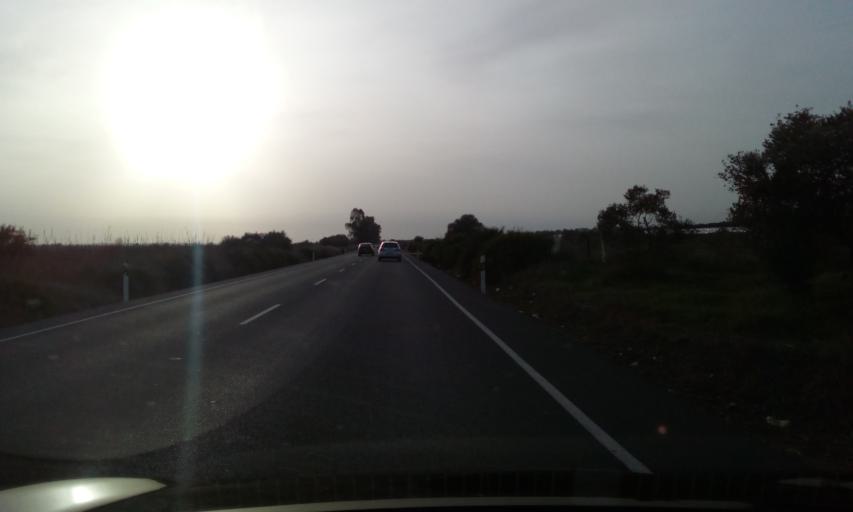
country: ES
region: Andalusia
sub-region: Provincia de Huelva
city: Niebla
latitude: 37.3474
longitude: -6.7154
